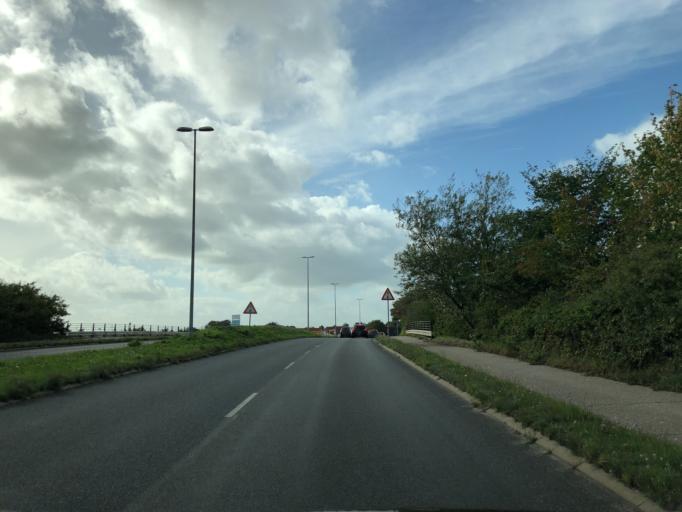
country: DK
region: Central Jutland
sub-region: Holstebro Kommune
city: Holstebro
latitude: 56.3597
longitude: 8.6046
